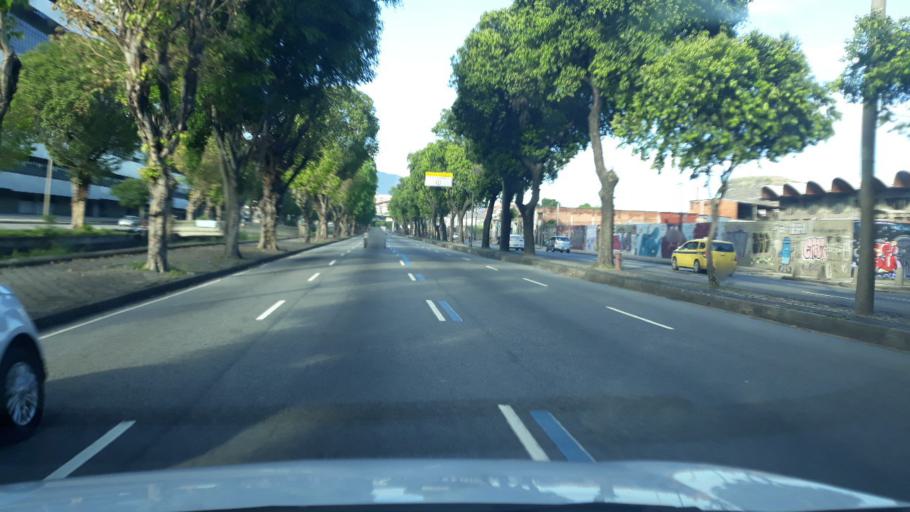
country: BR
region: Rio de Janeiro
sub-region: Rio De Janeiro
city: Rio de Janeiro
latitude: -22.9084
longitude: -43.2016
